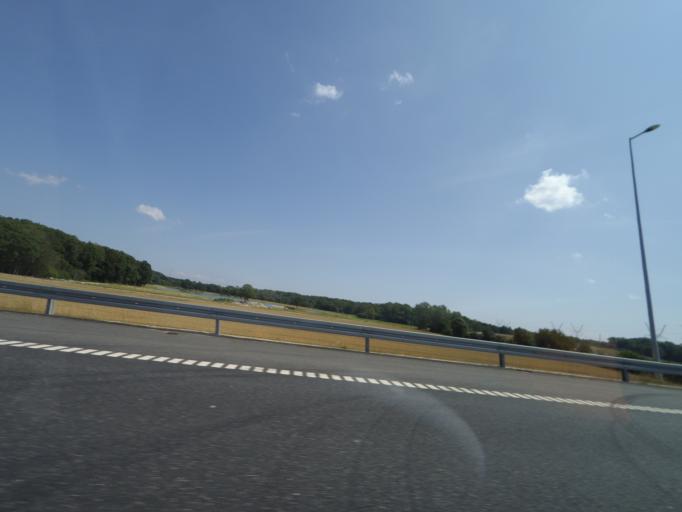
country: DK
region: South Denmark
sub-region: Odense Kommune
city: Hojby
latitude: 55.3509
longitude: 10.4229
